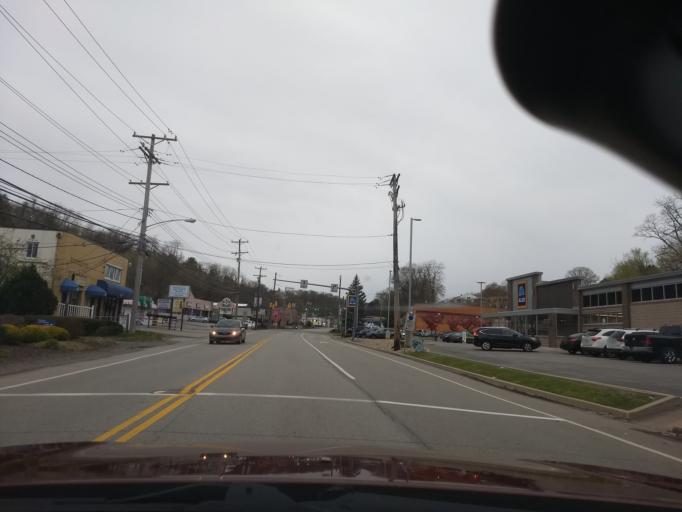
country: US
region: Pennsylvania
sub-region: Allegheny County
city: Castle Shannon
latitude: 40.3835
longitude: -80.0138
